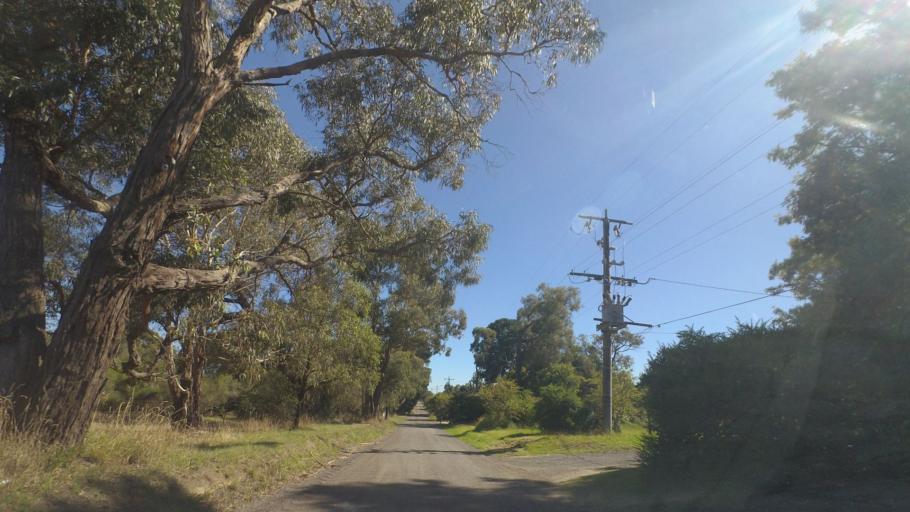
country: AU
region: Victoria
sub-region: Knox
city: Wantirna South
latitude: -37.8741
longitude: 145.2000
